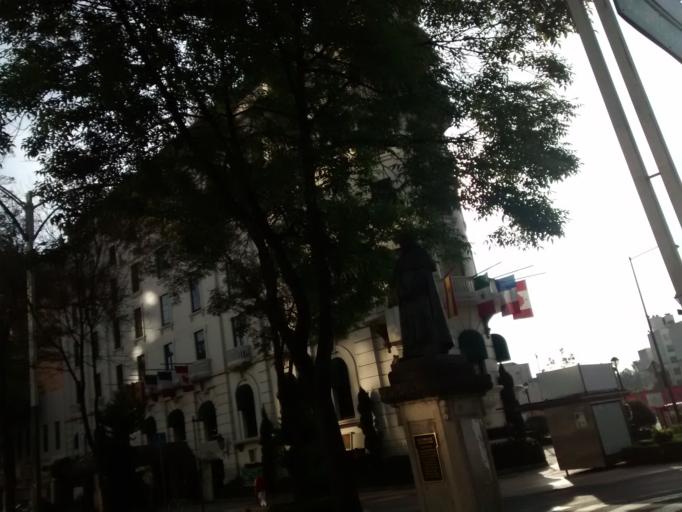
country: MX
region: Mexico City
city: Cuauhtemoc
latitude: 19.4334
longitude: -99.1541
